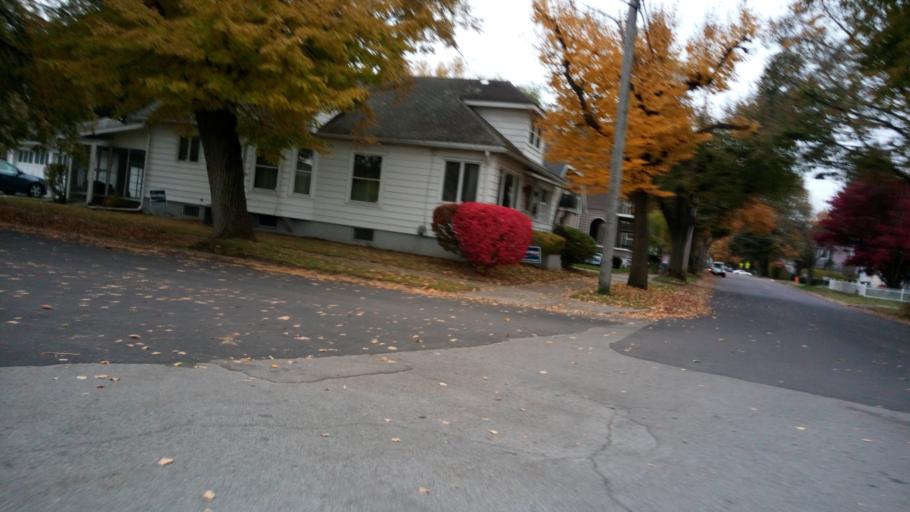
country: US
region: New York
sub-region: Chemung County
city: Elmira
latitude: 42.0841
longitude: -76.7924
